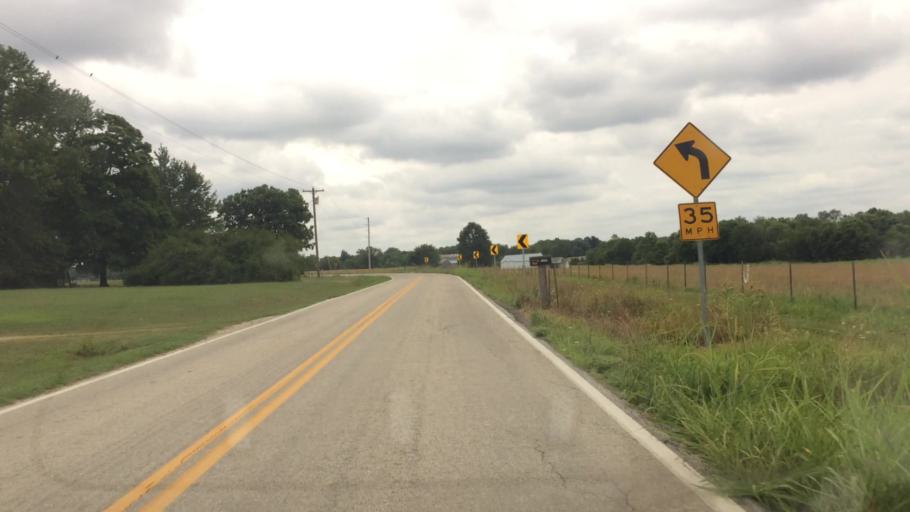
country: US
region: Missouri
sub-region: Greene County
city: Strafford
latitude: 37.2975
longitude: -93.1206
